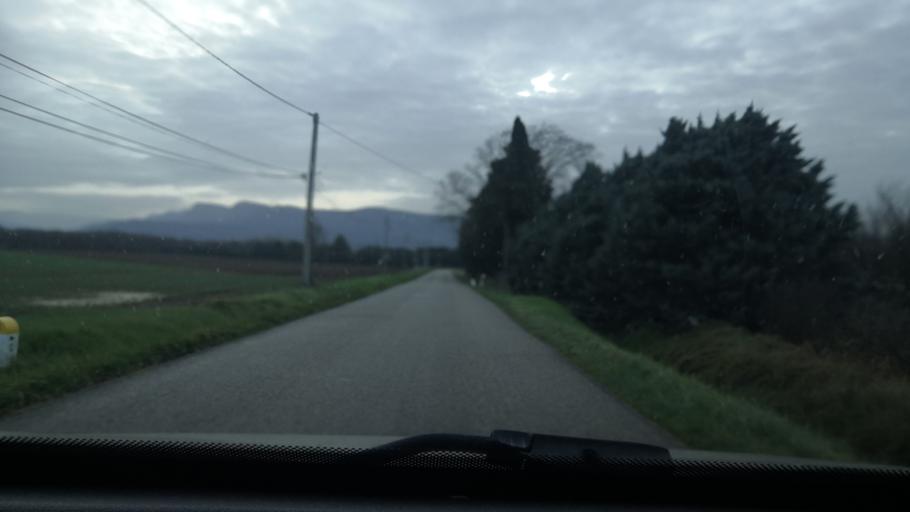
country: FR
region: Rhone-Alpes
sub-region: Departement de la Drome
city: La Begude-de-Mazenc
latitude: 44.5676
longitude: 4.9105
